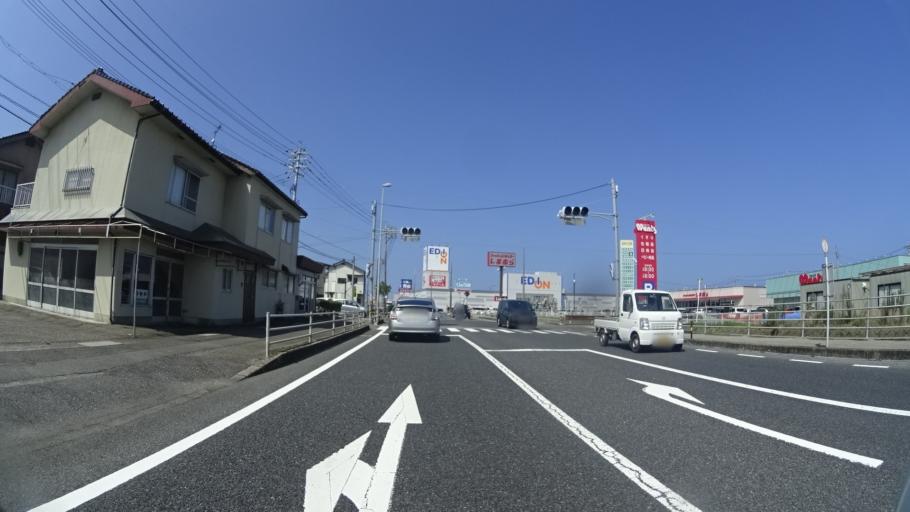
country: JP
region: Shimane
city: Masuda
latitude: 34.6890
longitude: 131.8225
